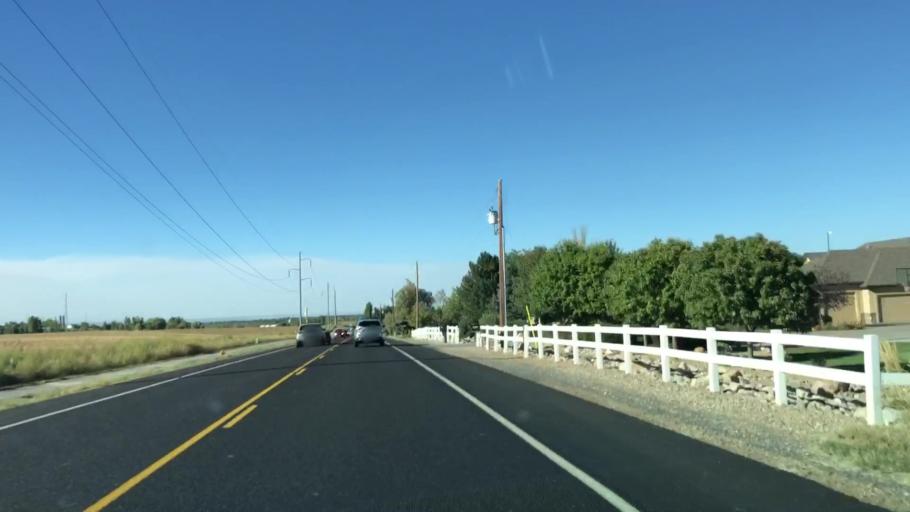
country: US
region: Colorado
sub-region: Larimer County
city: Loveland
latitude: 40.4595
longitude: -105.0441
